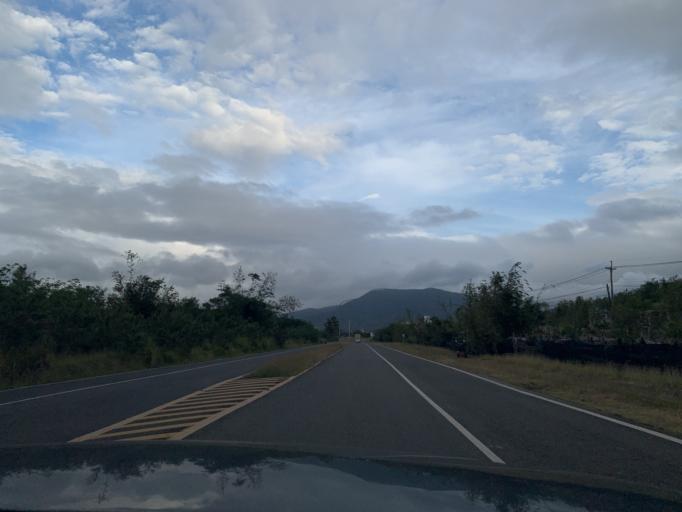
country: TW
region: Taiwan
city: Hengchun
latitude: 22.0522
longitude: 120.7154
